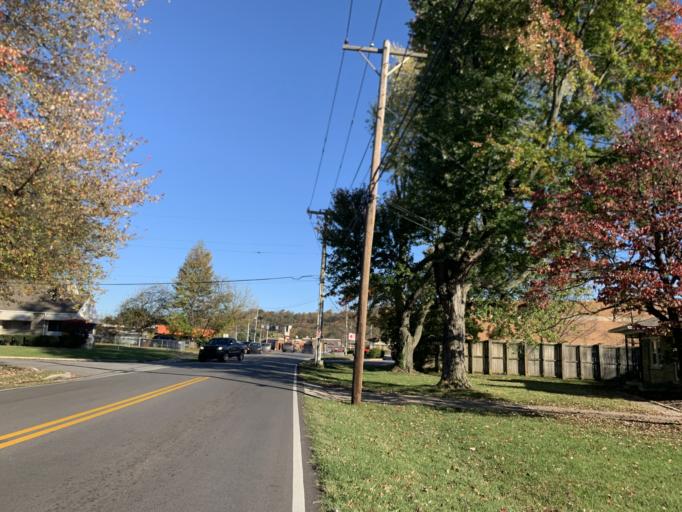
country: US
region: Kentucky
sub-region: Jefferson County
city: Saint Dennis
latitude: 38.1686
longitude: -85.8305
